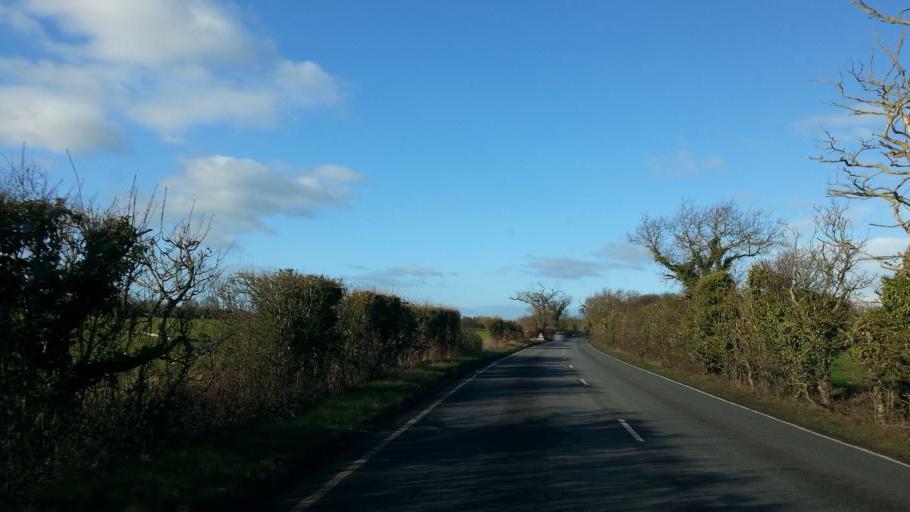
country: GB
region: England
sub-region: Suffolk
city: Halesworth
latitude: 52.2895
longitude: 1.5368
